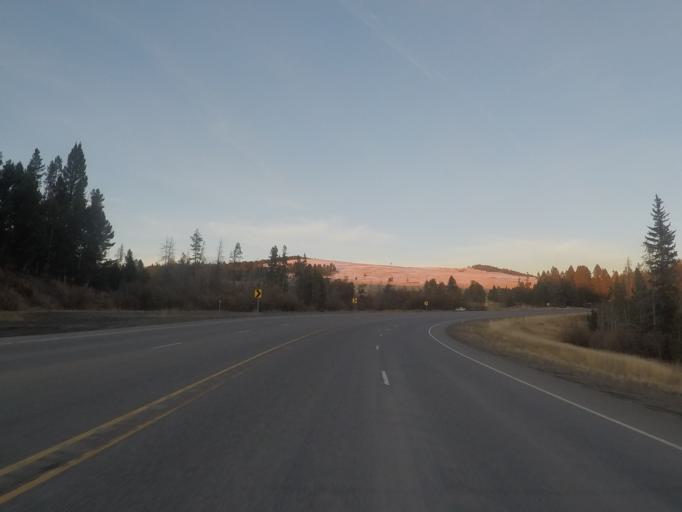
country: US
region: Montana
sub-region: Lewis and Clark County
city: Helena West Side
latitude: 46.5598
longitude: -112.3388
